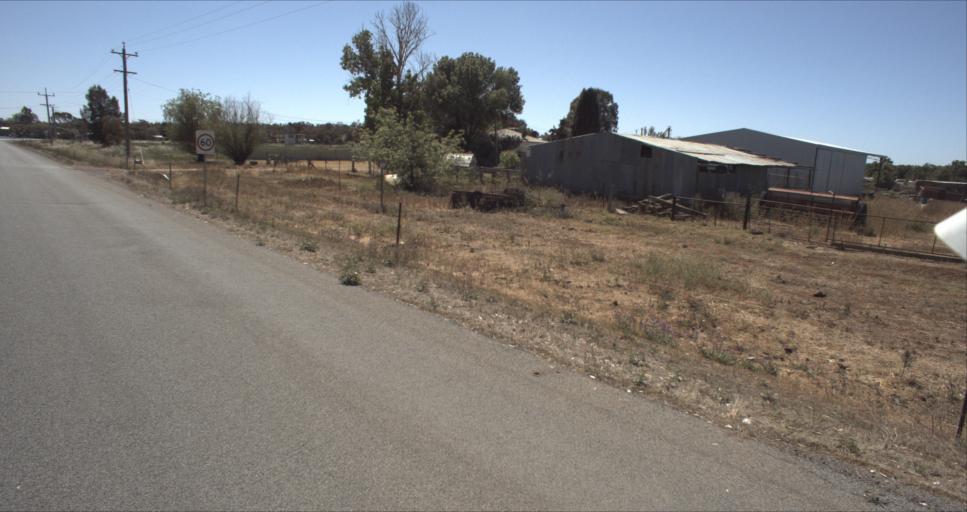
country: AU
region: New South Wales
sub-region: Leeton
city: Leeton
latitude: -34.4296
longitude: 146.2999
